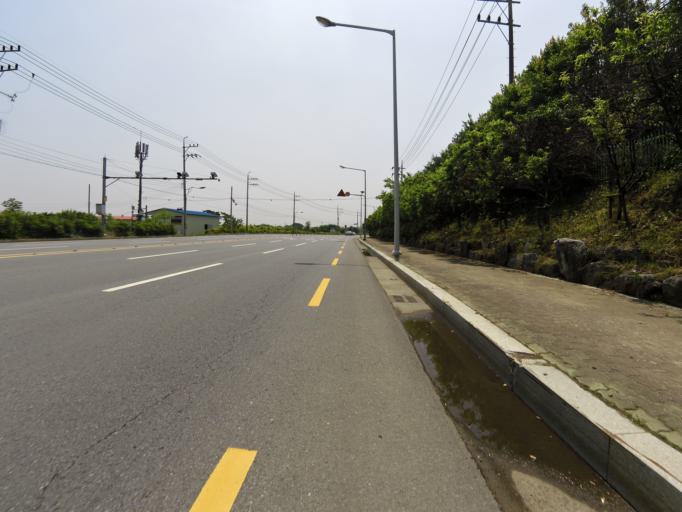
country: KR
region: Gyeongsangbuk-do
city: Gyeongsan-si
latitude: 35.8521
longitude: 128.7267
